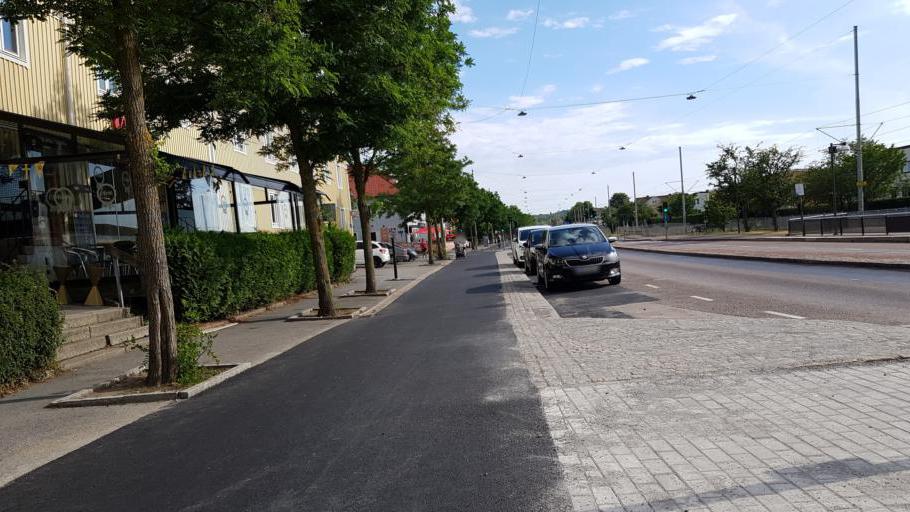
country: SE
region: Vaestra Goetaland
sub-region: Goteborg
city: Eriksbo
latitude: 57.7167
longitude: 12.0255
